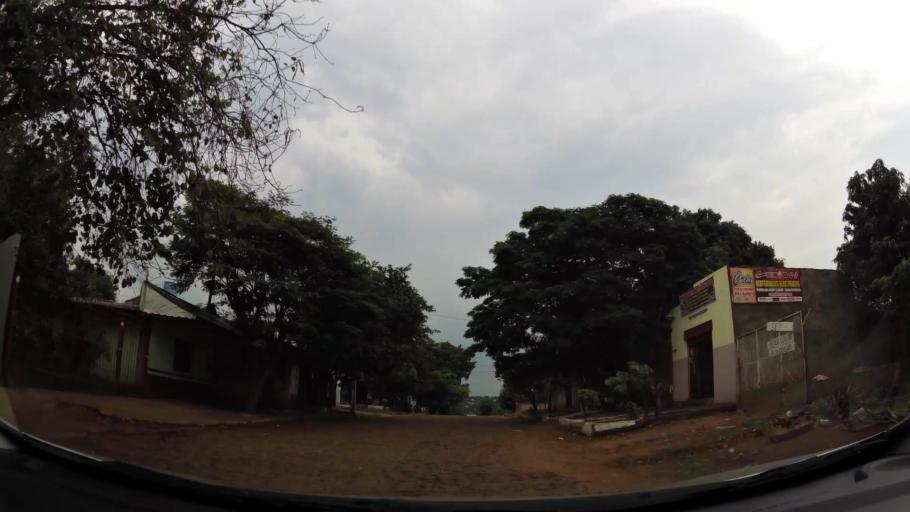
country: BR
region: Parana
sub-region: Foz Do Iguacu
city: Foz do Iguacu
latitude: -25.5468
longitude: -54.6020
